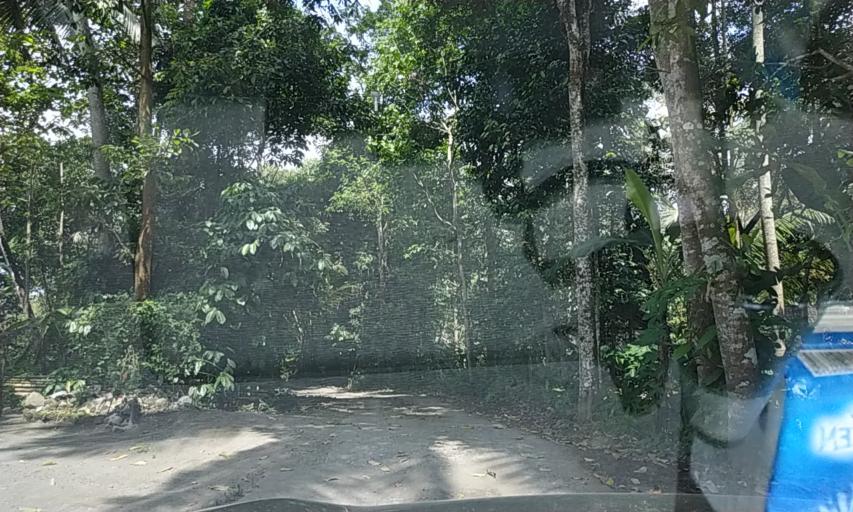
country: ID
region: Central Java
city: Jogonalan
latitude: -7.6333
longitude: 110.4853
